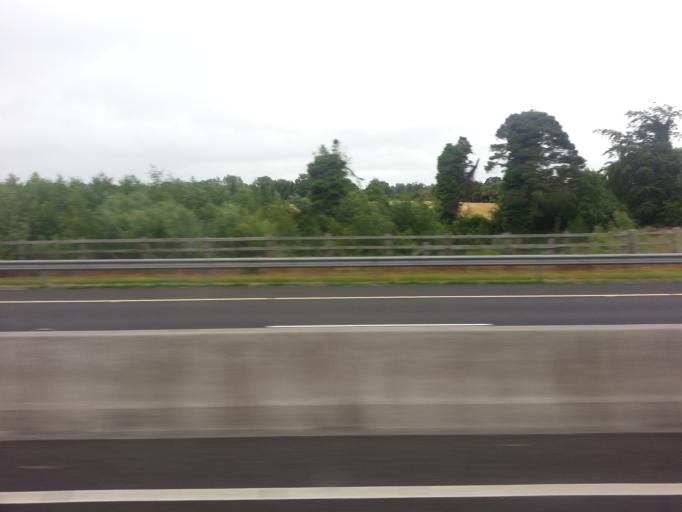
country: IE
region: Leinster
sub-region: Kildare
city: Castledermot
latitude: 52.9532
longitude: -6.8562
